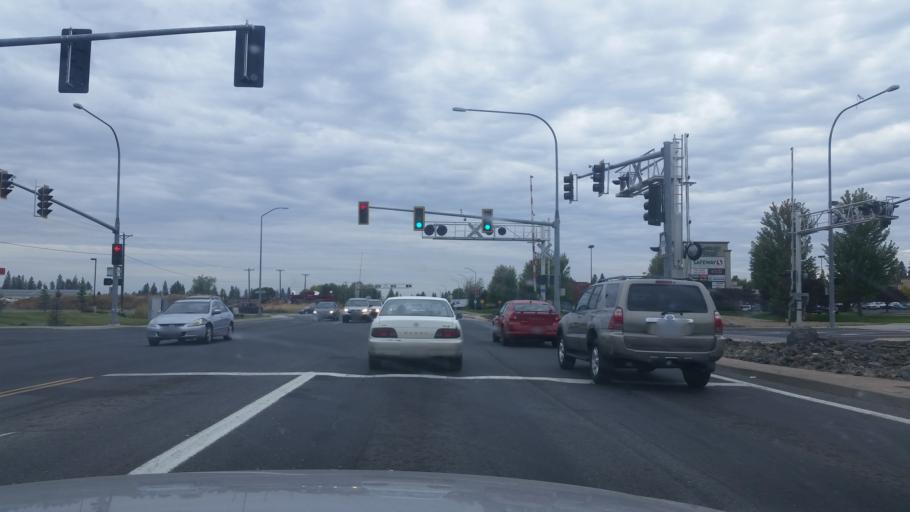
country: US
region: Washington
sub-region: Spokane County
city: Cheney
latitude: 47.5077
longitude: -117.5647
